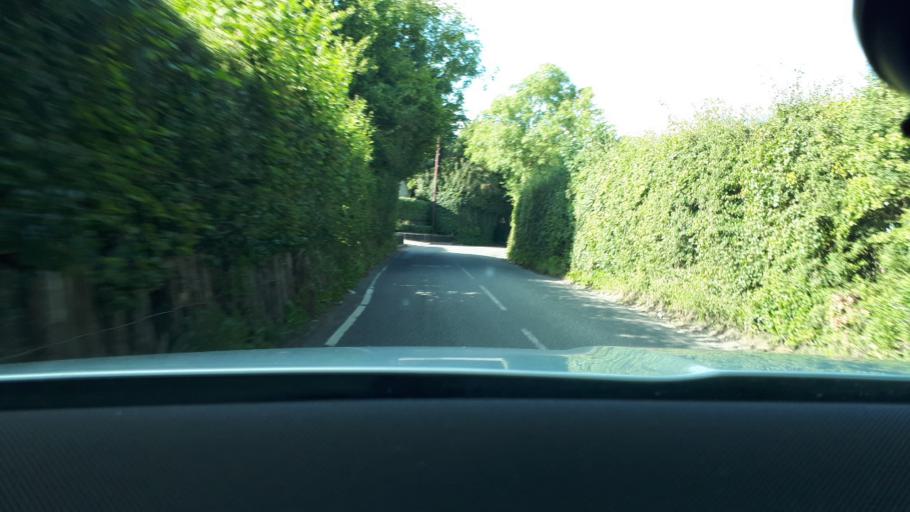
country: GB
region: England
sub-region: Kent
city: Biggin Hill
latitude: 51.3292
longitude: 0.0740
